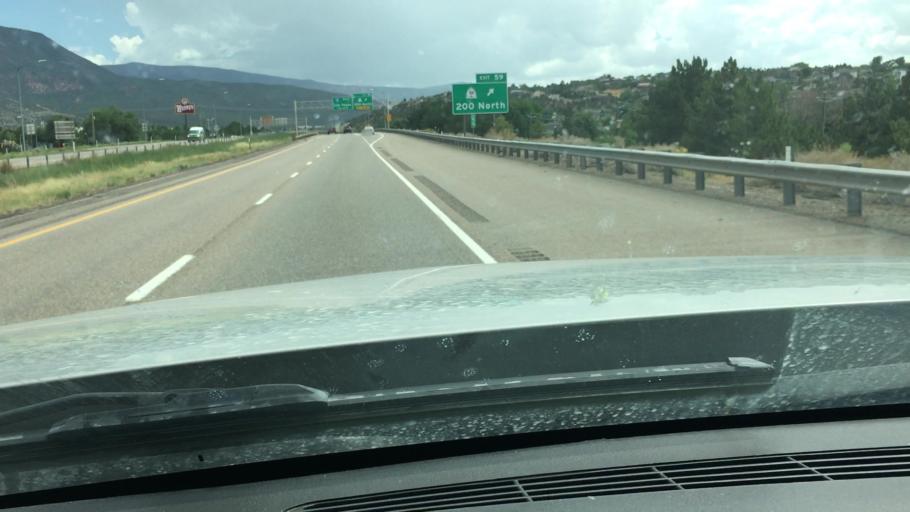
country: US
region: Utah
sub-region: Iron County
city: Cedar City
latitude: 37.6837
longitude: -113.0799
